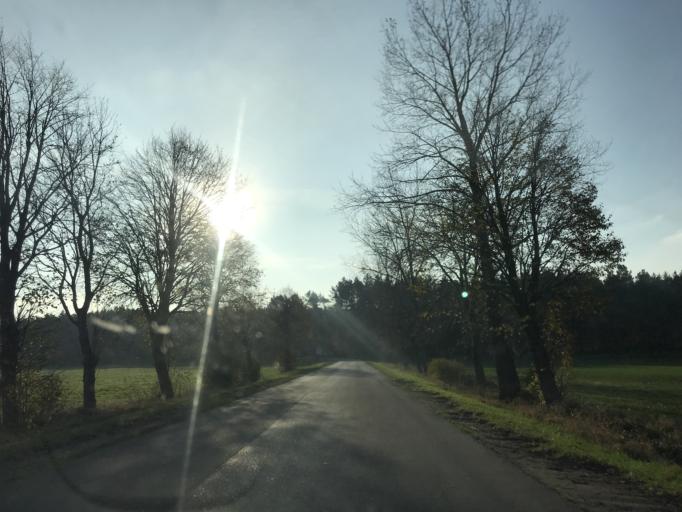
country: PL
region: Pomeranian Voivodeship
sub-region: Powiat pucki
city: Krokowa
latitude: 54.8055
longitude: 18.0992
